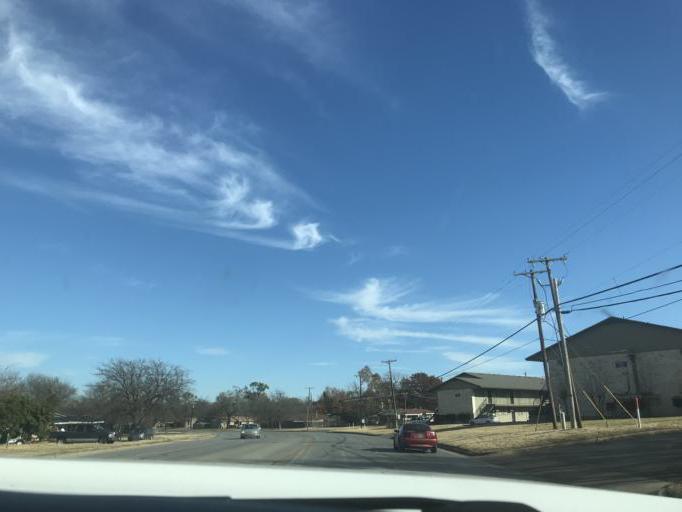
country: US
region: Texas
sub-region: Erath County
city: Stephenville
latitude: 32.2250
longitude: -98.2264
